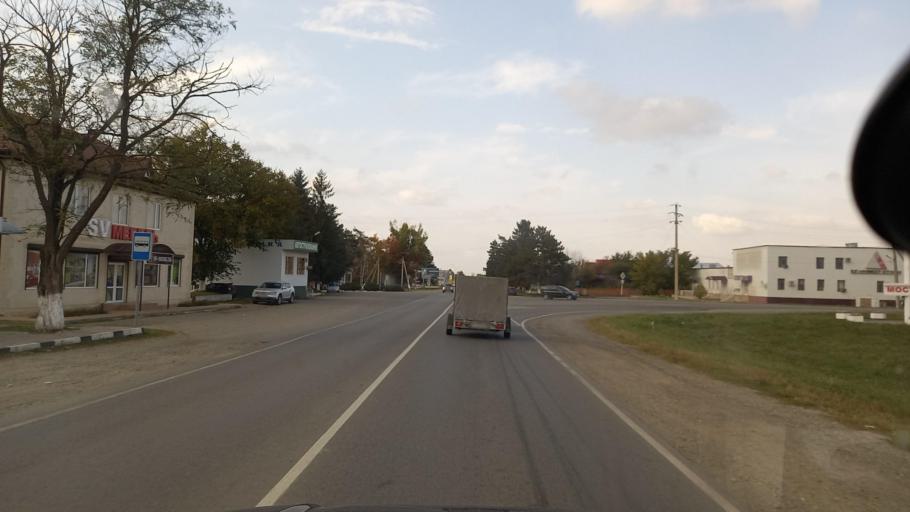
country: RU
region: Krasnodarskiy
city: Mostovskoy
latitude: 44.3968
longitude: 40.8119
